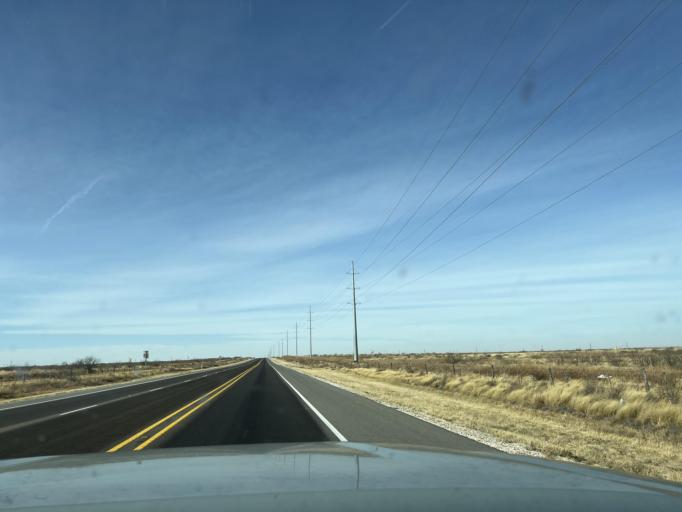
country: US
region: Texas
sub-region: Andrews County
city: Andrews
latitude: 32.3509
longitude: -102.7370
